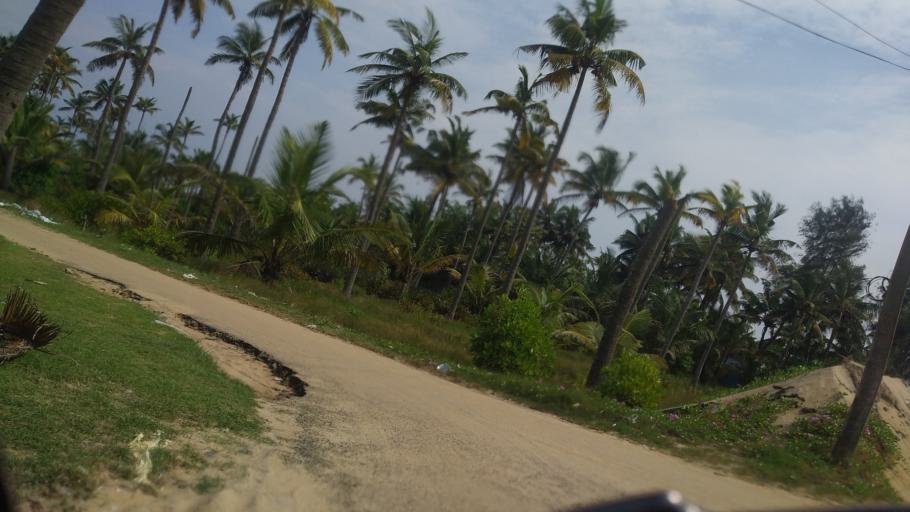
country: IN
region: Kerala
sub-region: Ernakulam
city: Elur
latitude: 10.0866
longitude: 76.1928
